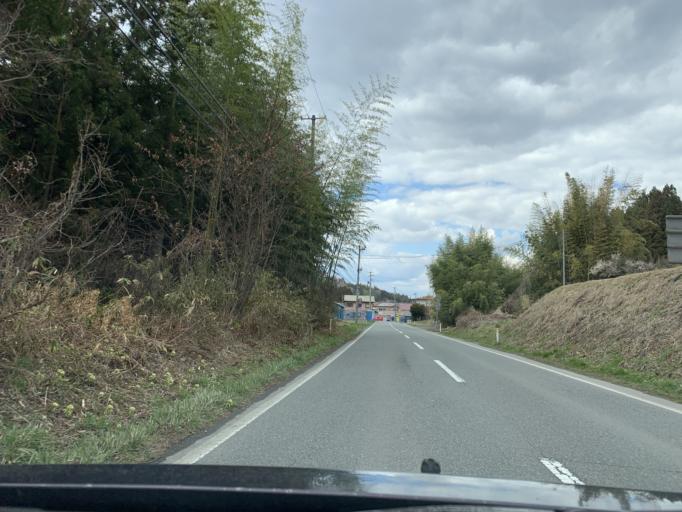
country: JP
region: Iwate
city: Ichinoseki
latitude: 38.8545
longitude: 141.3492
